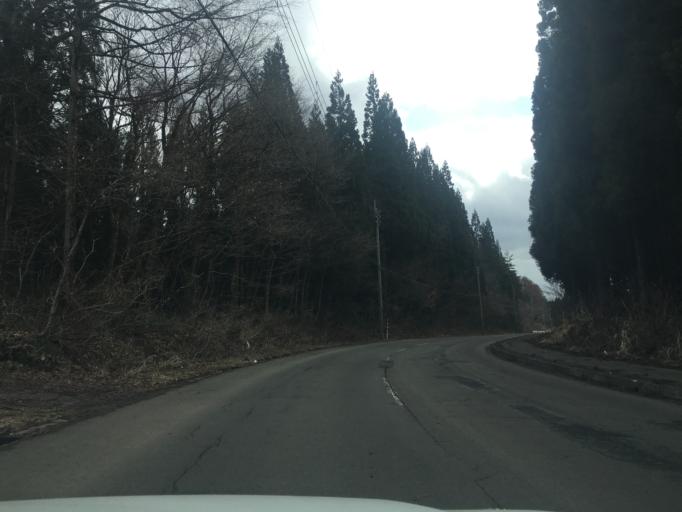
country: JP
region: Akita
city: Takanosu
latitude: 40.1853
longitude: 140.3537
